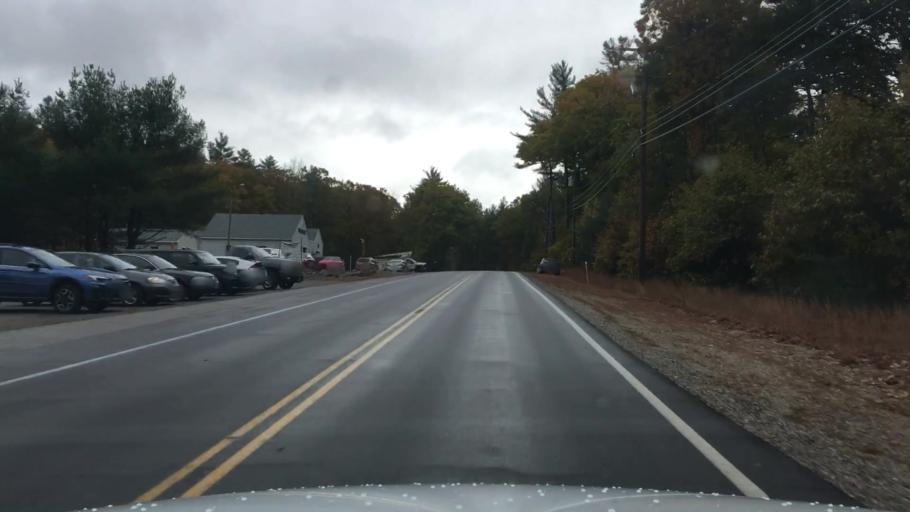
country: US
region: New Hampshire
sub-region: Strafford County
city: Lee
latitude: 43.1268
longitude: -71.0211
